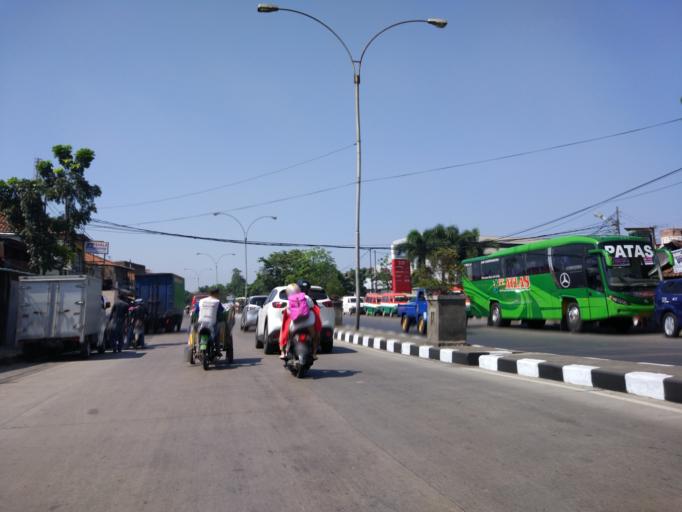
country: ID
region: West Java
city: Margahayukencana
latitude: -6.9408
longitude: 107.5821
